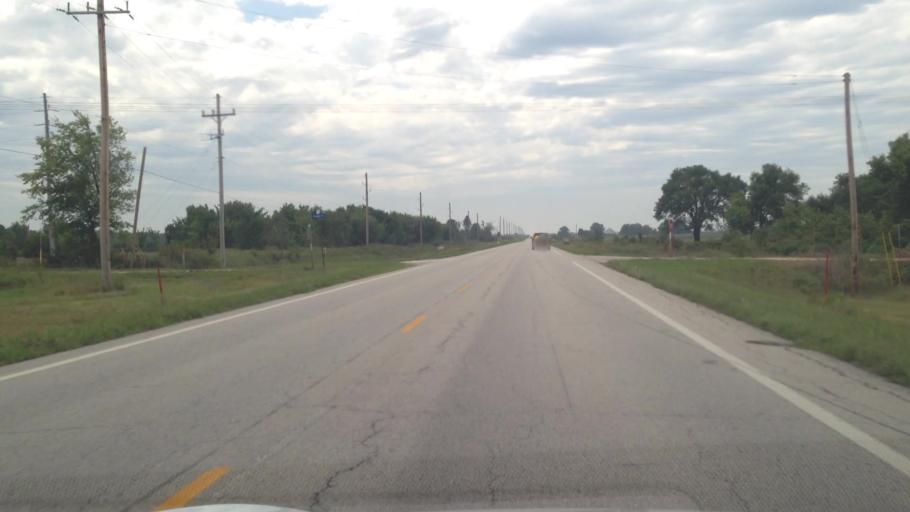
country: US
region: Kansas
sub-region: Allen County
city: Iola
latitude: 37.9511
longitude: -95.1700
